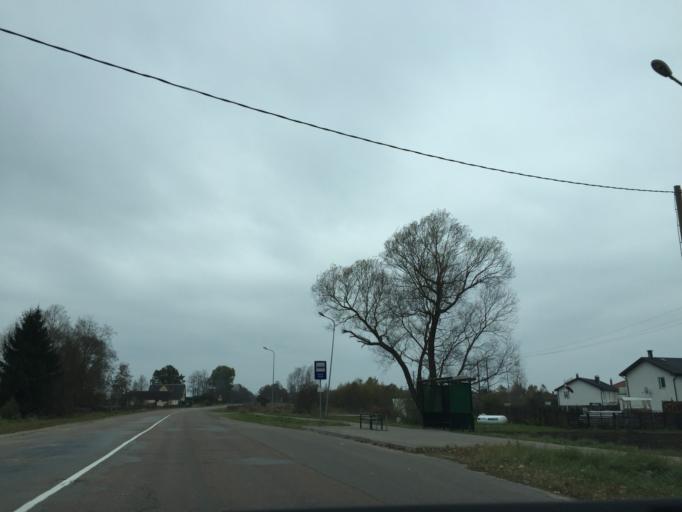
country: LV
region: Marupe
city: Marupe
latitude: 56.8456
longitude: 24.0466
